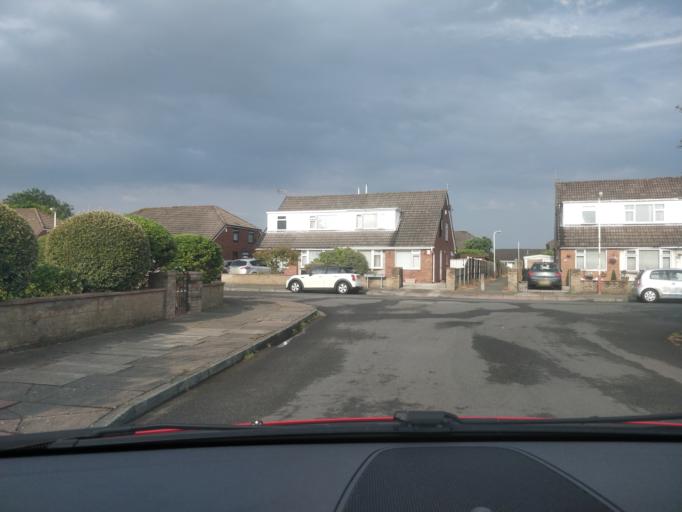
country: GB
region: England
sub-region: Lancashire
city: Banks
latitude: 53.6757
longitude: -2.9557
